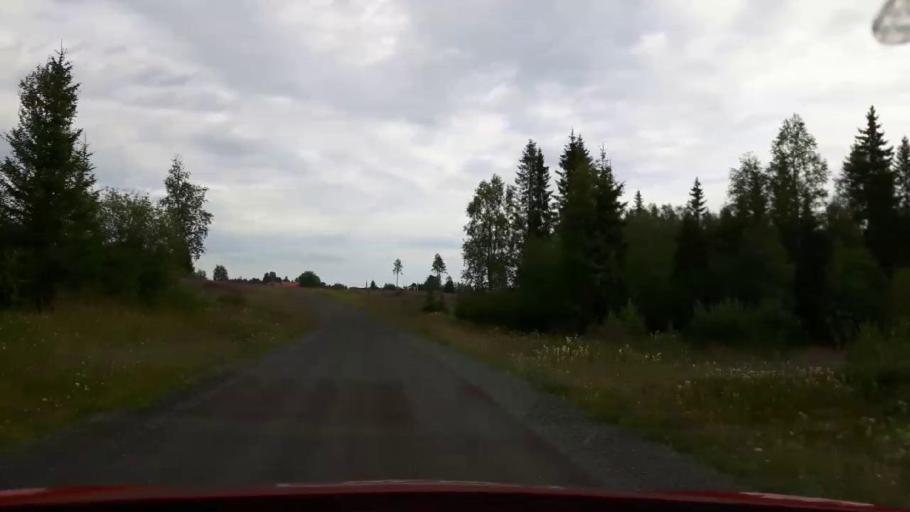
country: SE
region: Jaemtland
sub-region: OEstersunds Kommun
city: Lit
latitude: 63.4101
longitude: 15.2416
